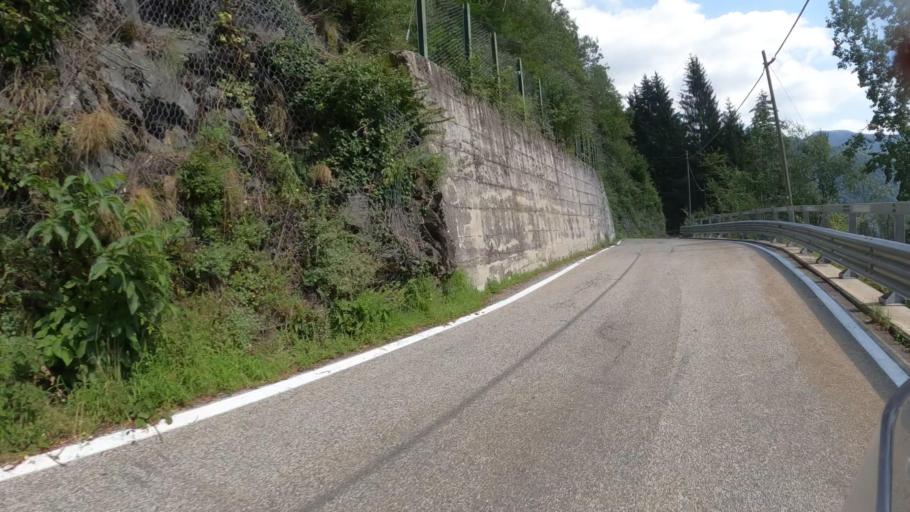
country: IT
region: Lombardy
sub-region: Provincia di Varese
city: Veddasca
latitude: 46.0764
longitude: 8.8023
